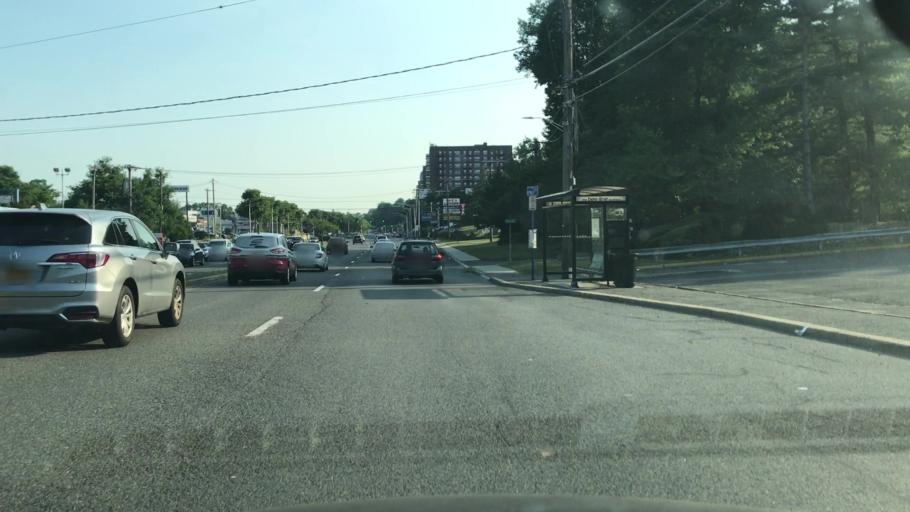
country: US
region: New York
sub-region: Westchester County
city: Greenville
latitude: 40.9877
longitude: -73.8243
